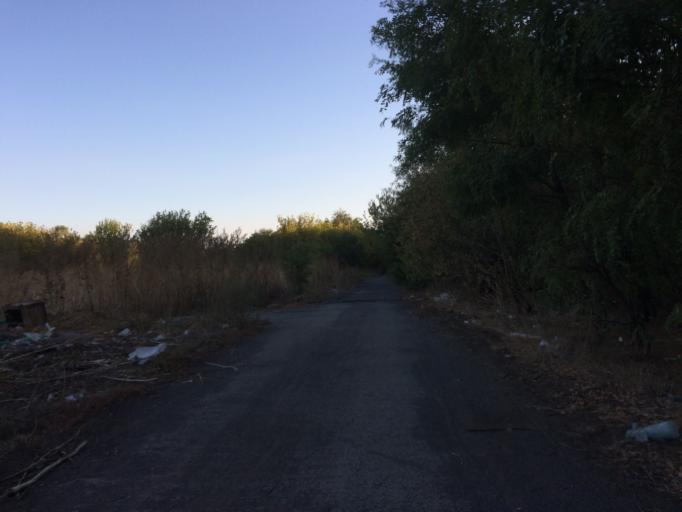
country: RU
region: Rostov
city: Gigant
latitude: 46.5149
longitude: 41.1945
